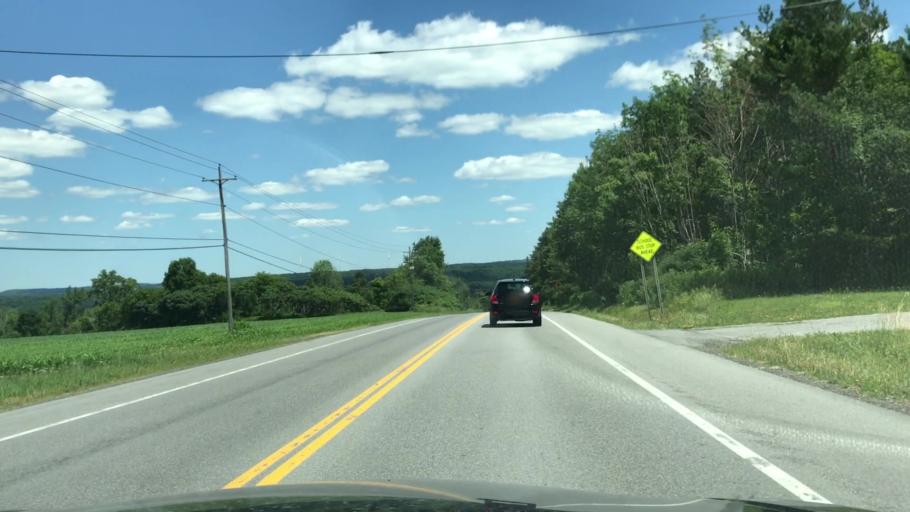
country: US
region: New York
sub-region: Wyoming County
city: Attica
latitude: 42.7704
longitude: -78.3413
